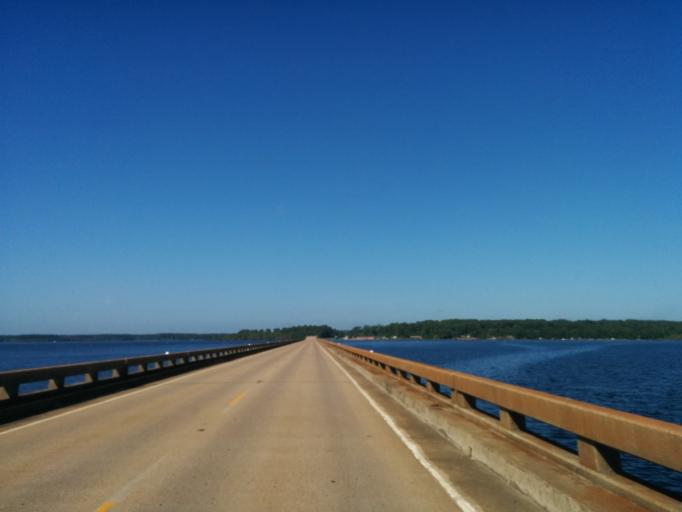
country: US
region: Texas
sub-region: Sabine County
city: Milam
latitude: 31.4708
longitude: -93.7381
